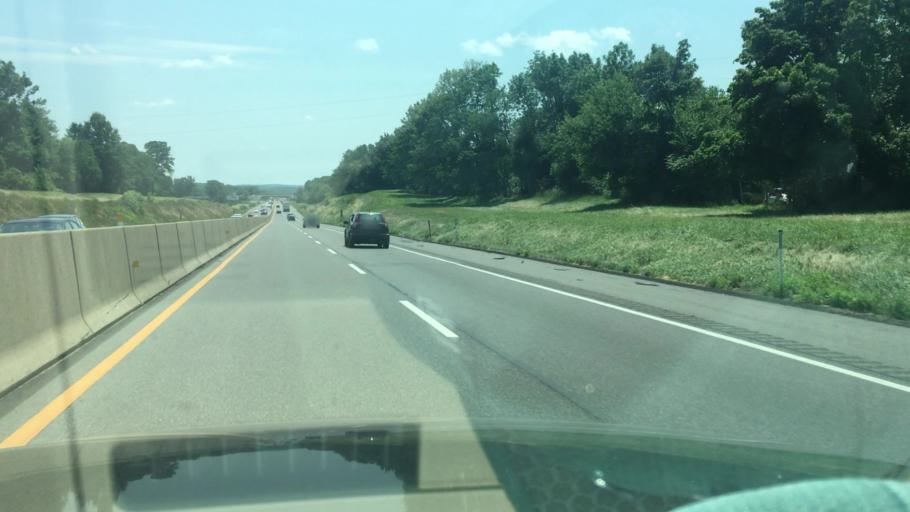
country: US
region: Pennsylvania
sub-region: Bucks County
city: Spinnerstown
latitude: 40.4538
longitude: -75.4390
